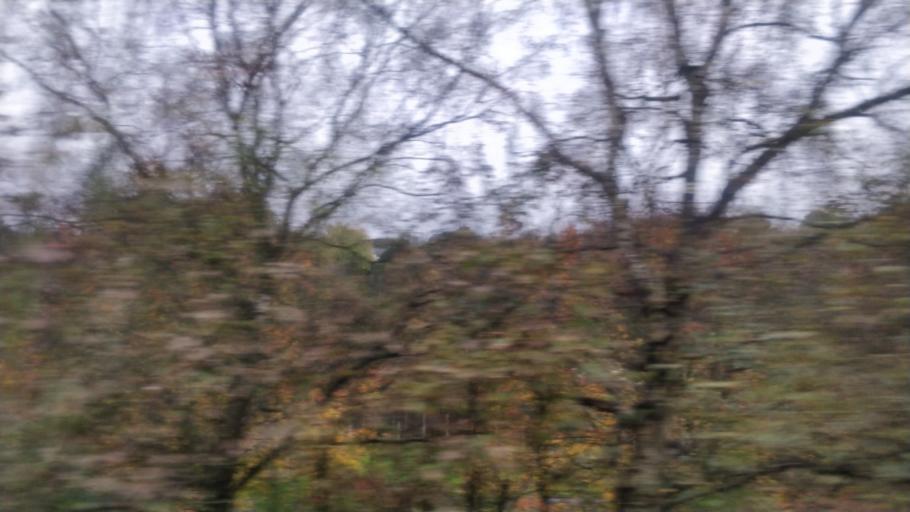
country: GB
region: England
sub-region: Borough of Wigan
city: Shevington
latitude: 53.5605
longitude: -2.6979
